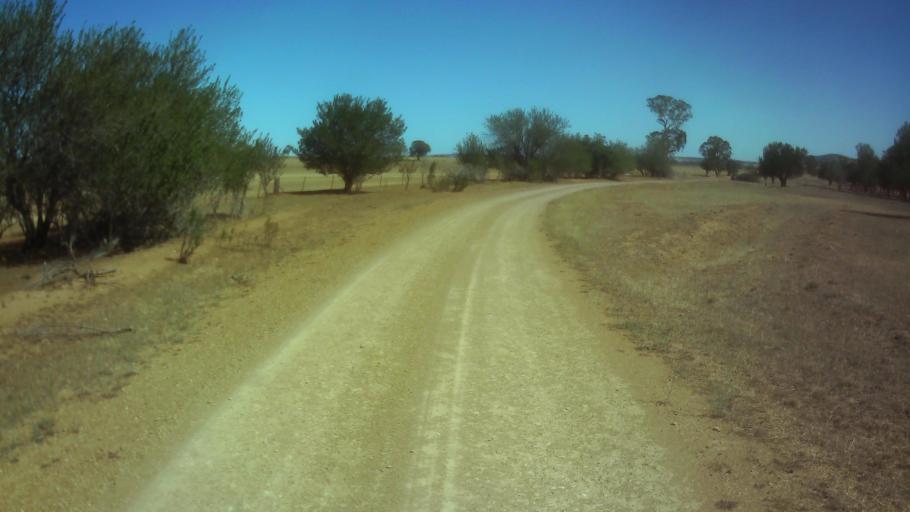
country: AU
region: New South Wales
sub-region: Weddin
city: Grenfell
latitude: -33.9615
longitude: 148.3050
